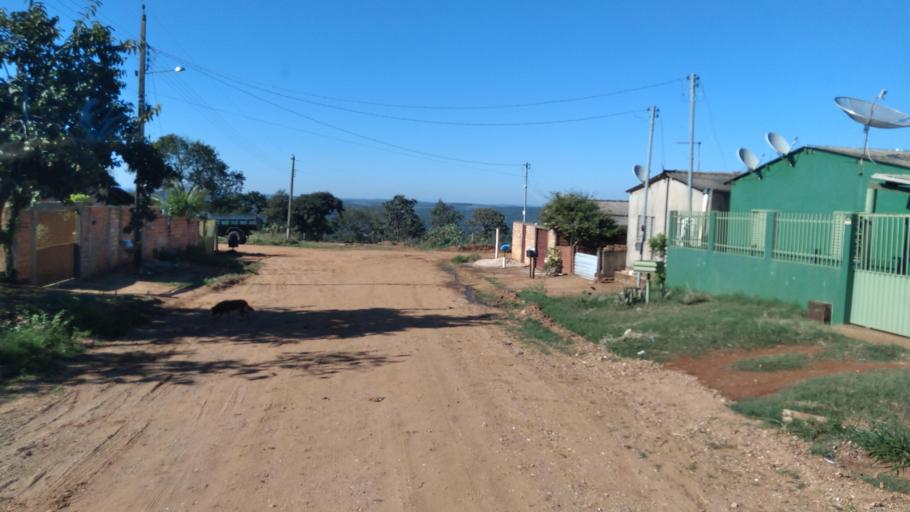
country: BR
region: Goias
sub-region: Mineiros
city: Mineiros
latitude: -17.5937
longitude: -52.5547
